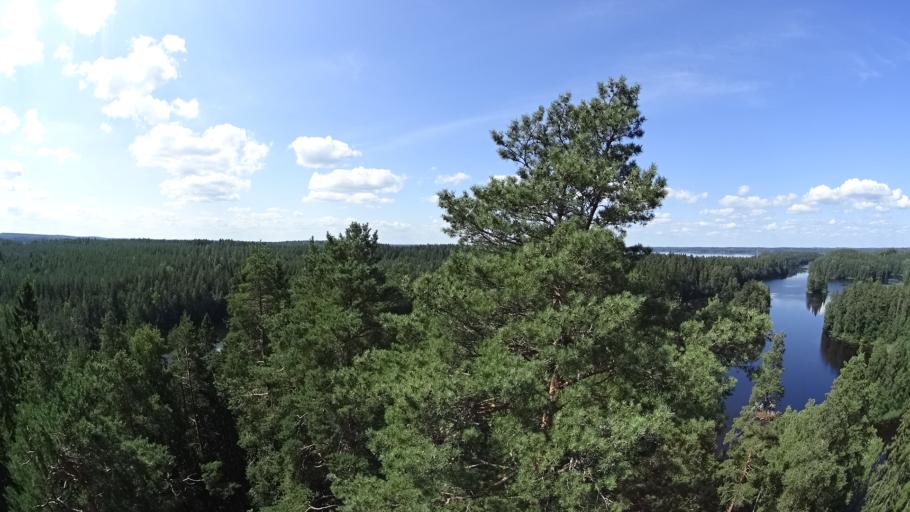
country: FI
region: Haeme
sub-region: Forssa
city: Tammela
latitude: 60.7757
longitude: 23.8339
